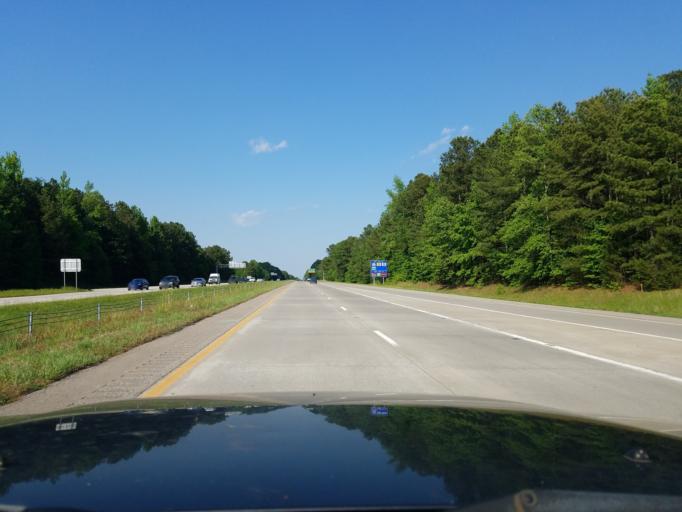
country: US
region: North Carolina
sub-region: Vance County
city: South Henderson
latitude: 36.3284
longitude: -78.4468
